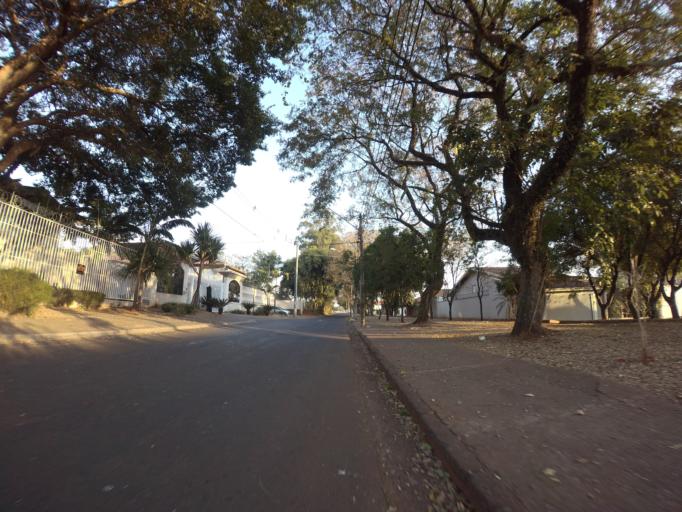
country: BR
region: Sao Paulo
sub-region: Piracicaba
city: Piracicaba
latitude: -22.7674
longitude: -47.5919
